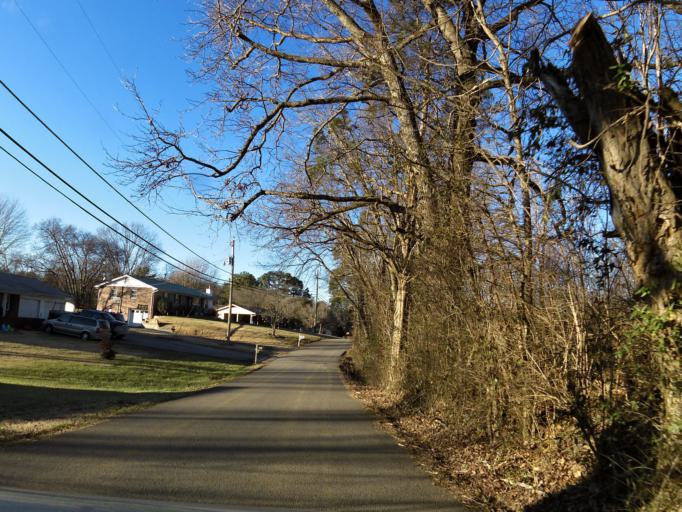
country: US
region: Tennessee
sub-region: Knox County
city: Knoxville
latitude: 35.9208
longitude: -83.8551
